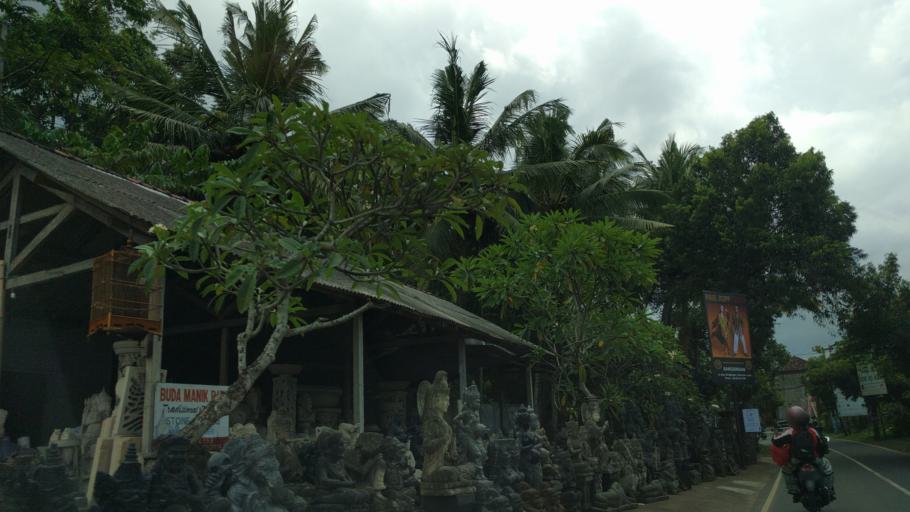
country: ID
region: Bali
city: Banjar Tebongkang
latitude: -8.5298
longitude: 115.2440
